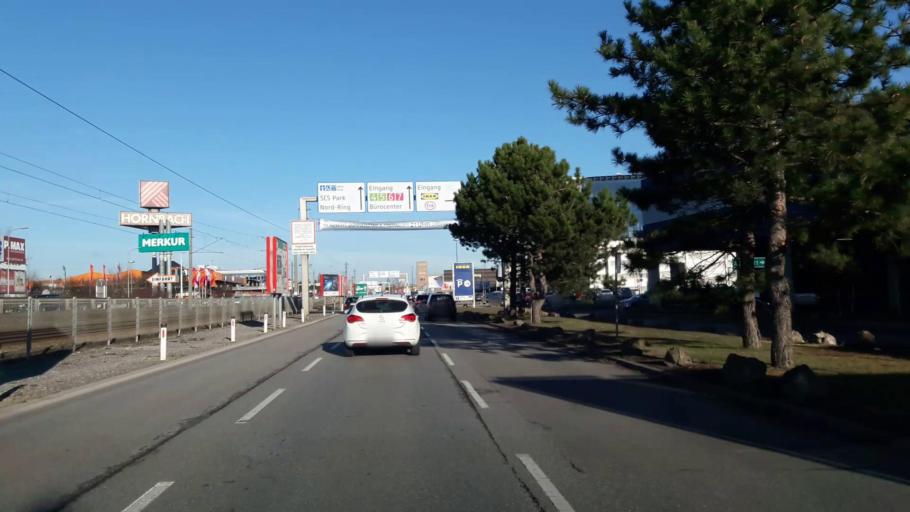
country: AT
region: Lower Austria
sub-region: Politischer Bezirk Modling
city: Wiener Neudorf
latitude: 48.1061
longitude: 16.3157
